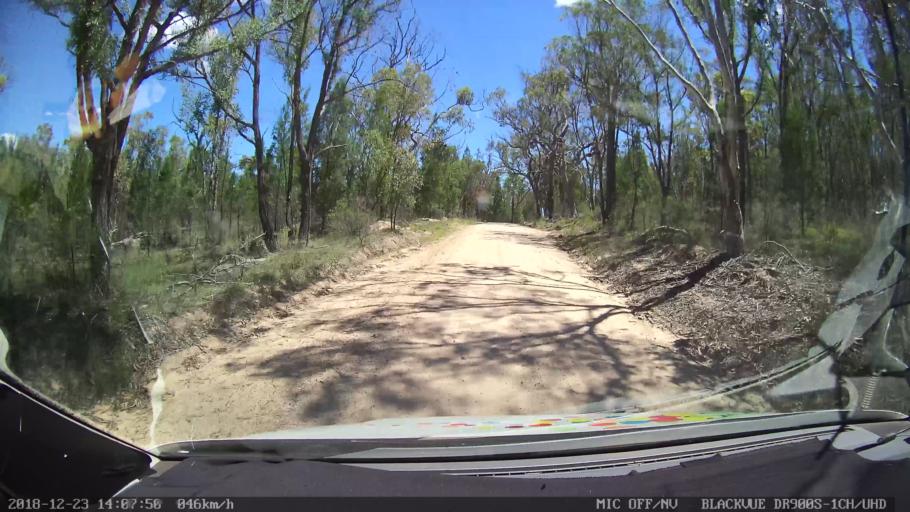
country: AU
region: New South Wales
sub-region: Tamworth Municipality
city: Manilla
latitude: -30.6386
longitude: 151.0709
